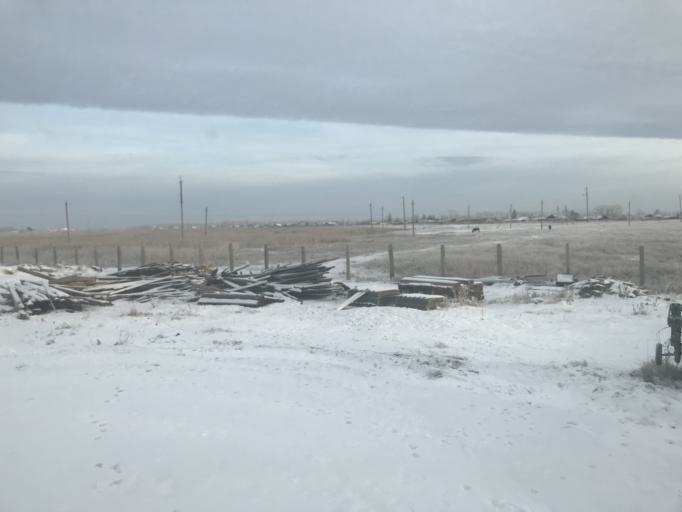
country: KZ
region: Soltustik Qazaqstan
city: Smirnovo
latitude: 54.8476
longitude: 69.7206
